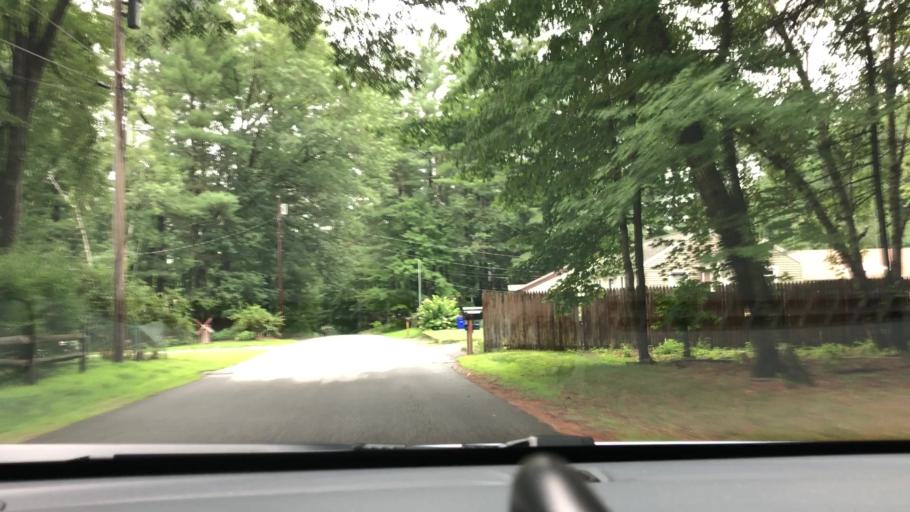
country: US
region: New Hampshire
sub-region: Hillsborough County
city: Pinardville
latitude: 43.0080
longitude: -71.5195
